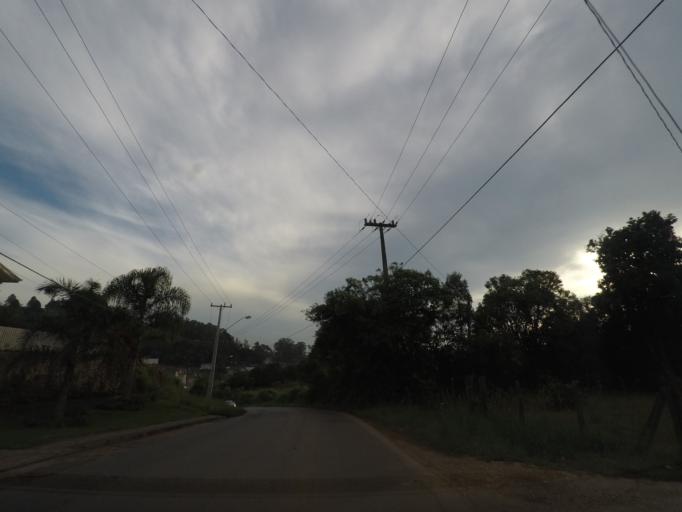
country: BR
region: Parana
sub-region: Colombo
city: Colombo
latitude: -25.2871
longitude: -49.2137
